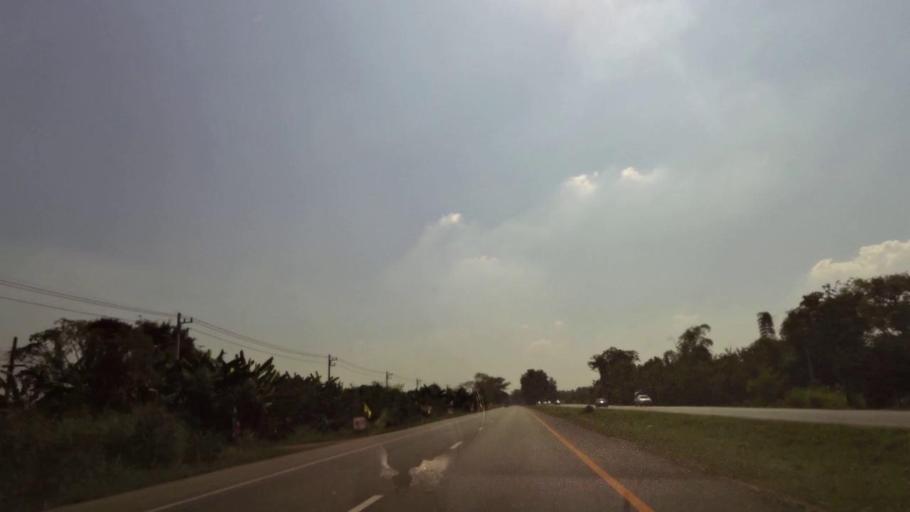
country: TH
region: Phichit
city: Bueng Na Rang
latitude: 16.2391
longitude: 100.1254
